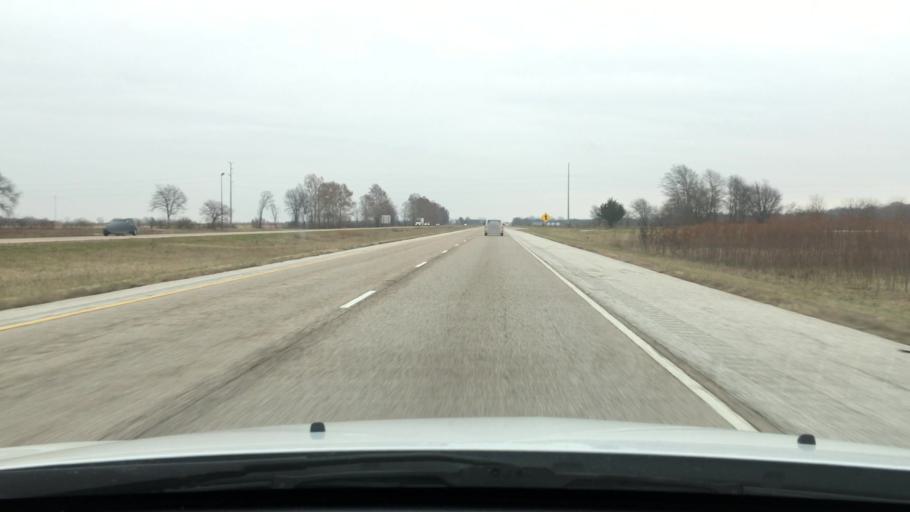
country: US
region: Illinois
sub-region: Scott County
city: Winchester
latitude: 39.6811
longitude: -90.4545
